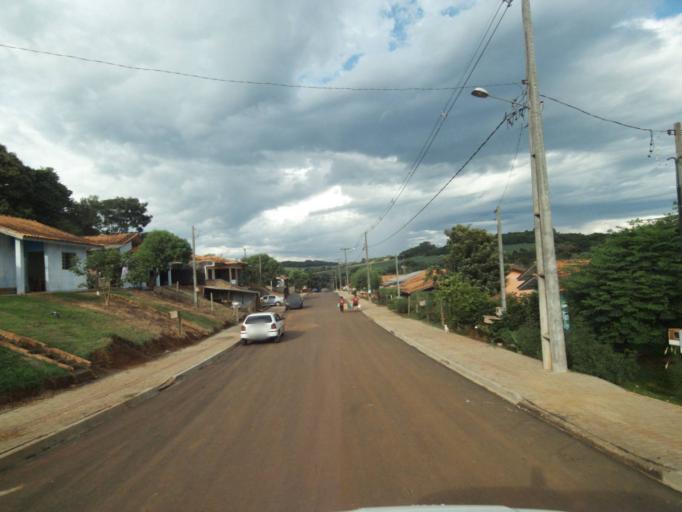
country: BR
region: Parana
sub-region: Laranjeiras Do Sul
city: Laranjeiras do Sul
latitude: -25.4953
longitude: -52.5253
